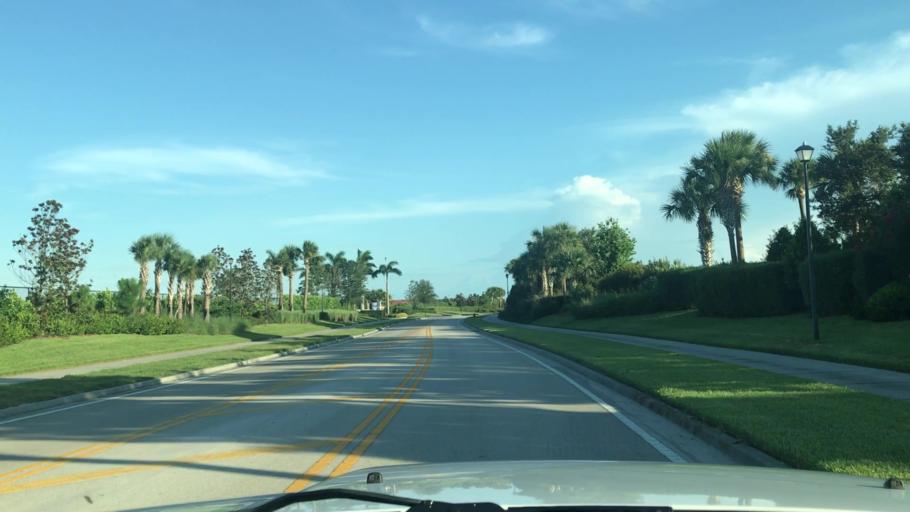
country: US
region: Florida
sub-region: Indian River County
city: Gifford
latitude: 27.6912
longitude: -80.4350
